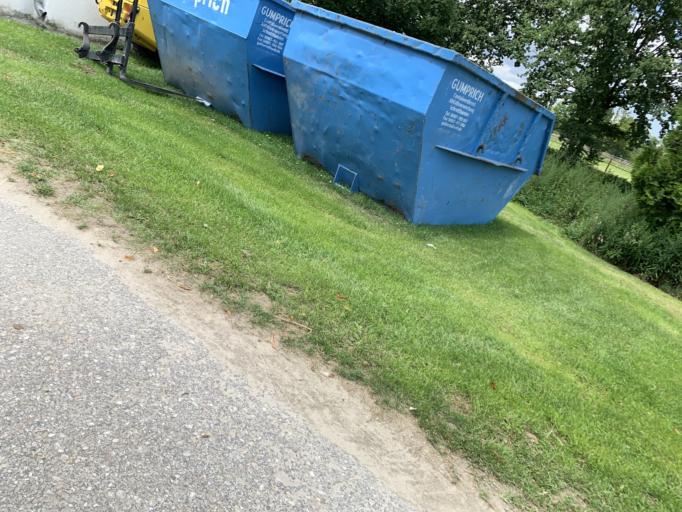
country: DE
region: Bavaria
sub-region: Upper Bavaria
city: Zolling
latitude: 48.4416
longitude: 11.7873
